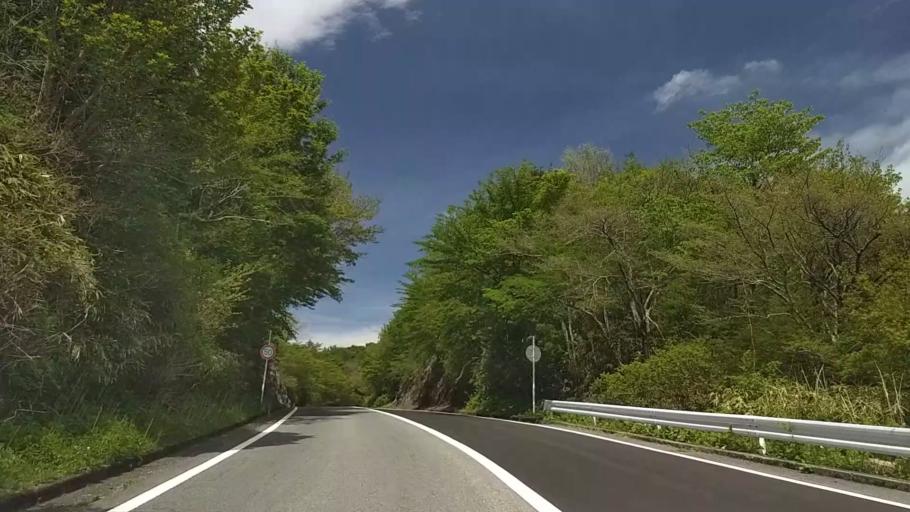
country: JP
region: Kanagawa
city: Hakone
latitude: 35.1936
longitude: 139.0652
